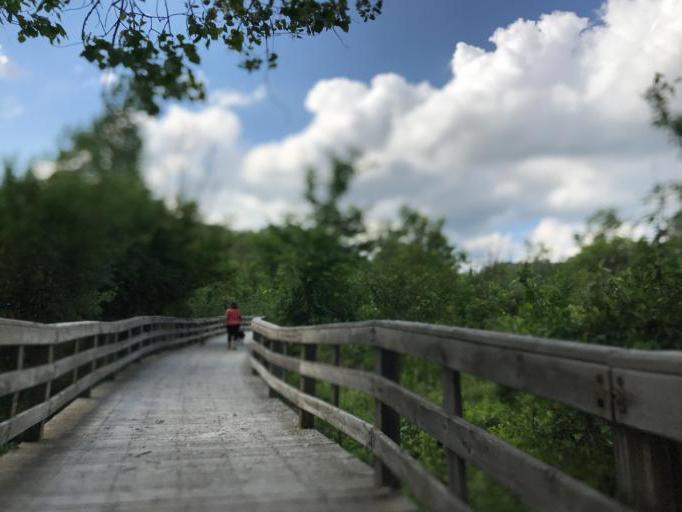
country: US
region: Michigan
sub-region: Oakland County
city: South Lyon
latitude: 42.4549
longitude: -83.6616
